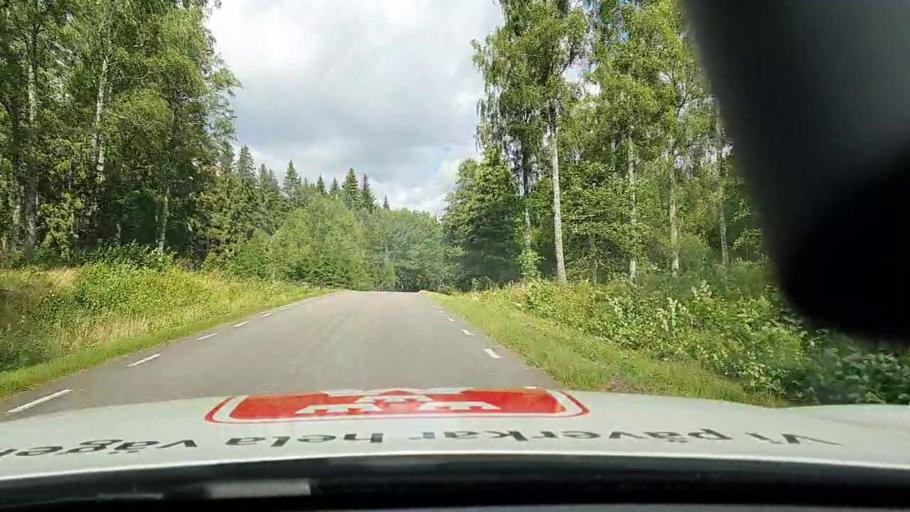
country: SE
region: Vaestra Goetaland
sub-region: Karlsborgs Kommun
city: Molltorp
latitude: 58.6076
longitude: 14.3182
